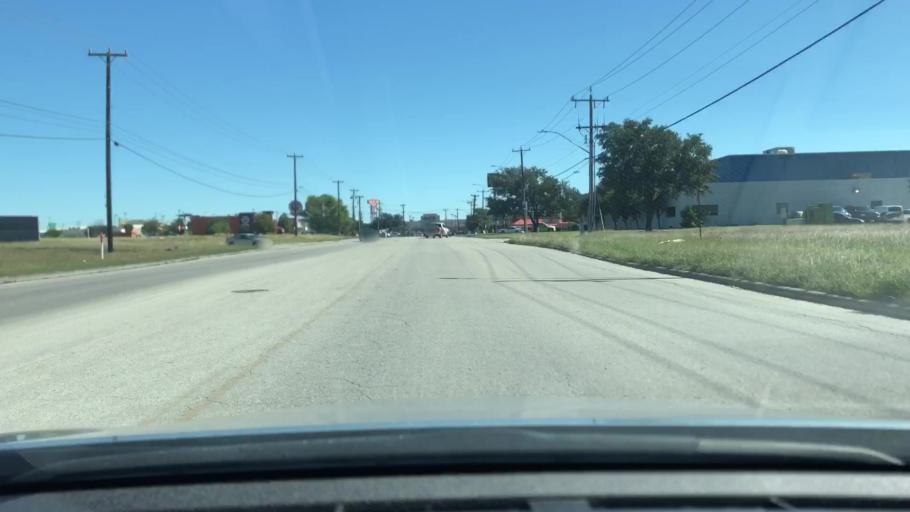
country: US
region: Texas
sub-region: Bexar County
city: Kirby
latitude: 29.4752
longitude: -98.3572
